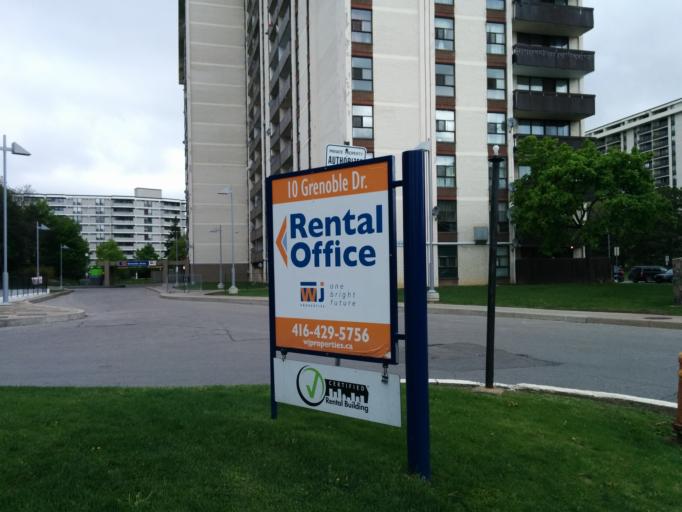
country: CA
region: Ontario
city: Willowdale
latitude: 43.7159
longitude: -79.3340
